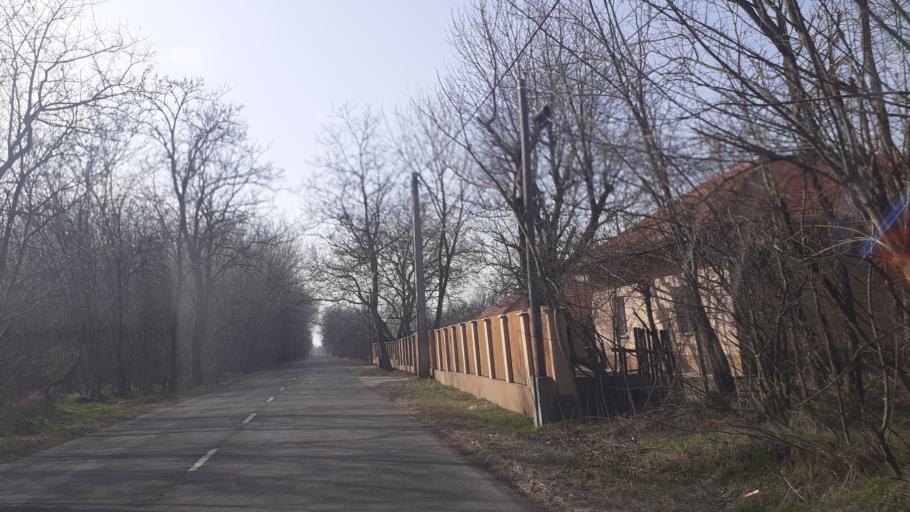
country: HU
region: Pest
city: Orkeny
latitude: 47.1194
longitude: 19.4145
